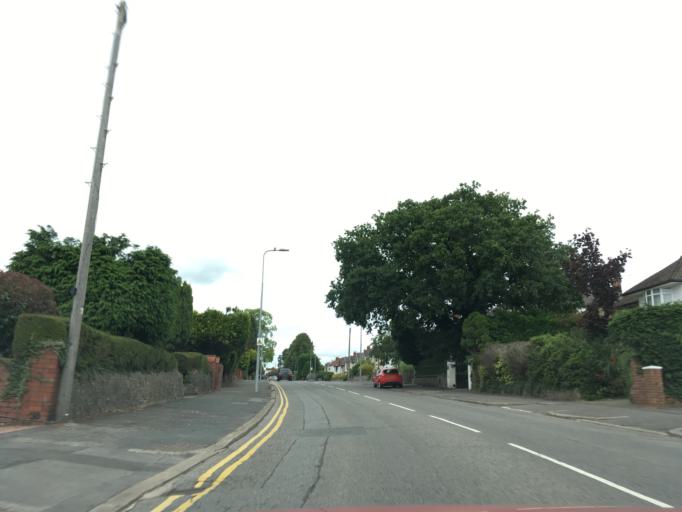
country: GB
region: Wales
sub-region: Cardiff
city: Cardiff
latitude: 51.5130
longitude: -3.1639
